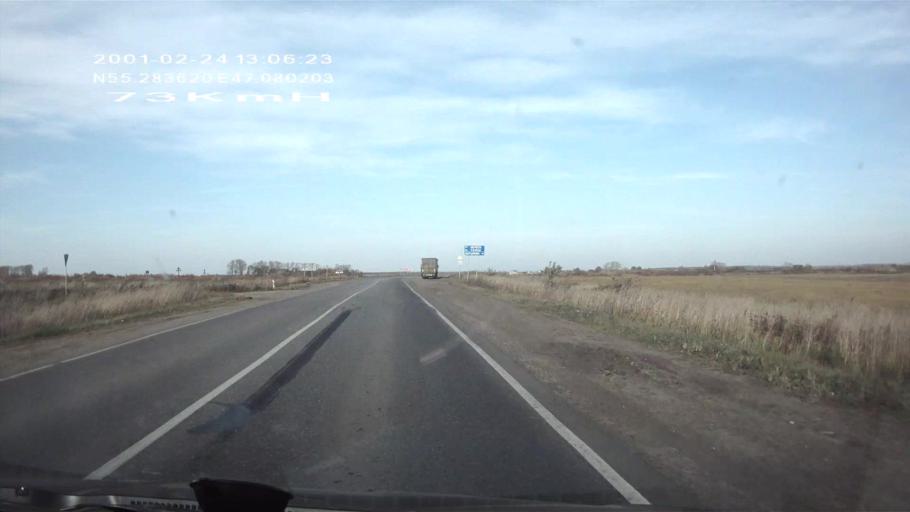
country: RU
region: Chuvashia
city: Ibresi
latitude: 55.2836
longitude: 47.0802
